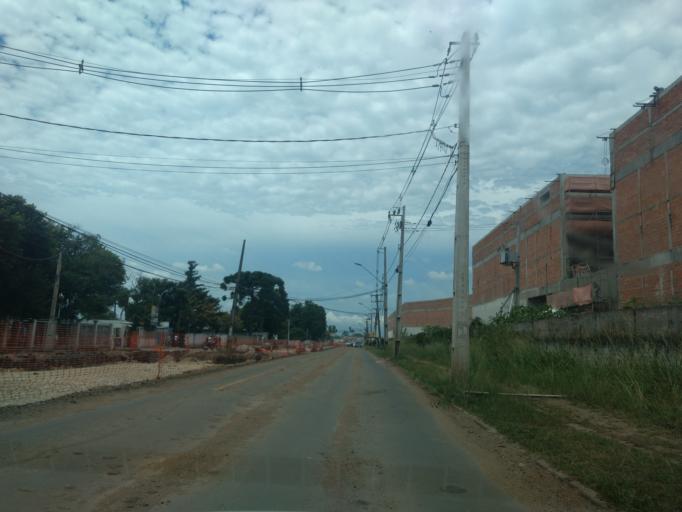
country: BR
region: Parana
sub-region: Pinhais
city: Pinhais
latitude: -25.4264
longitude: -49.2151
